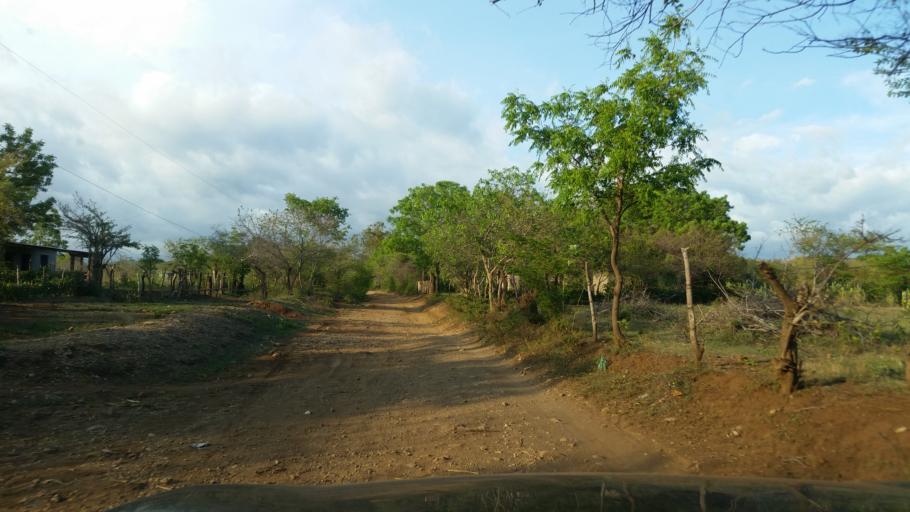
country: NI
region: Managua
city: Masachapa
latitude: 11.7785
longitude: -86.4765
